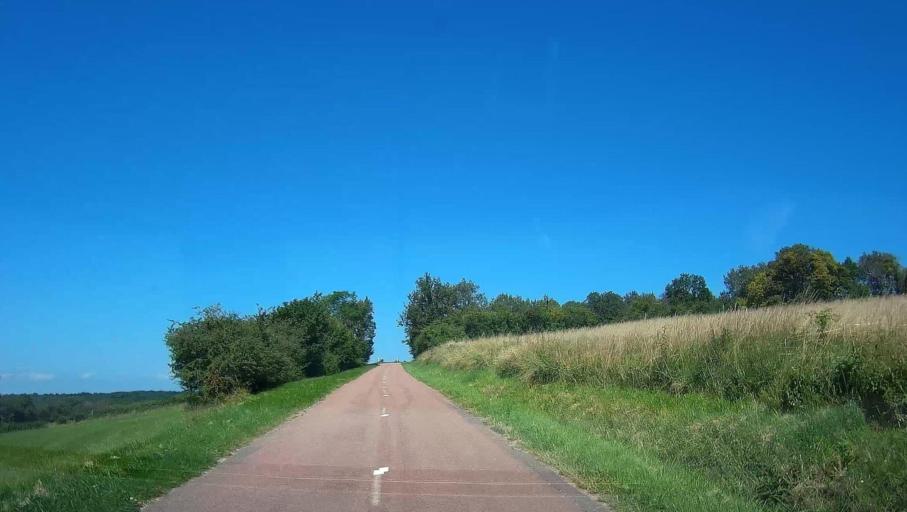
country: FR
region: Bourgogne
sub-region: Departement de la Cote-d'Or
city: Nolay
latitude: 46.9775
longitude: 4.6616
